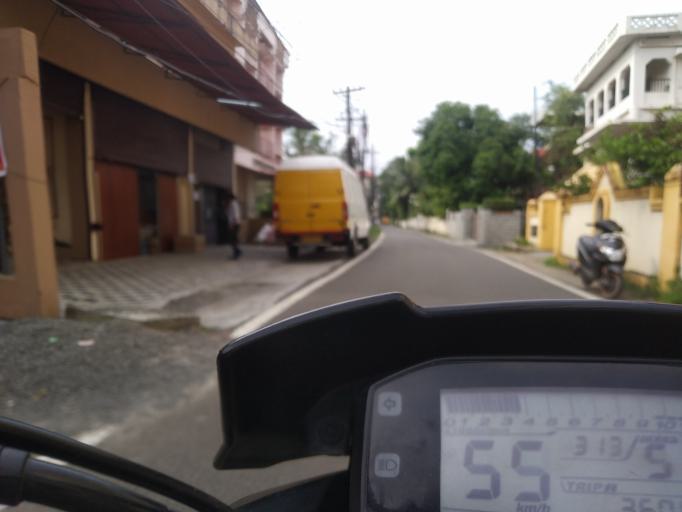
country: IN
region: Kerala
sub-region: Ernakulam
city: Cochin
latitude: 9.9747
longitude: 76.2871
